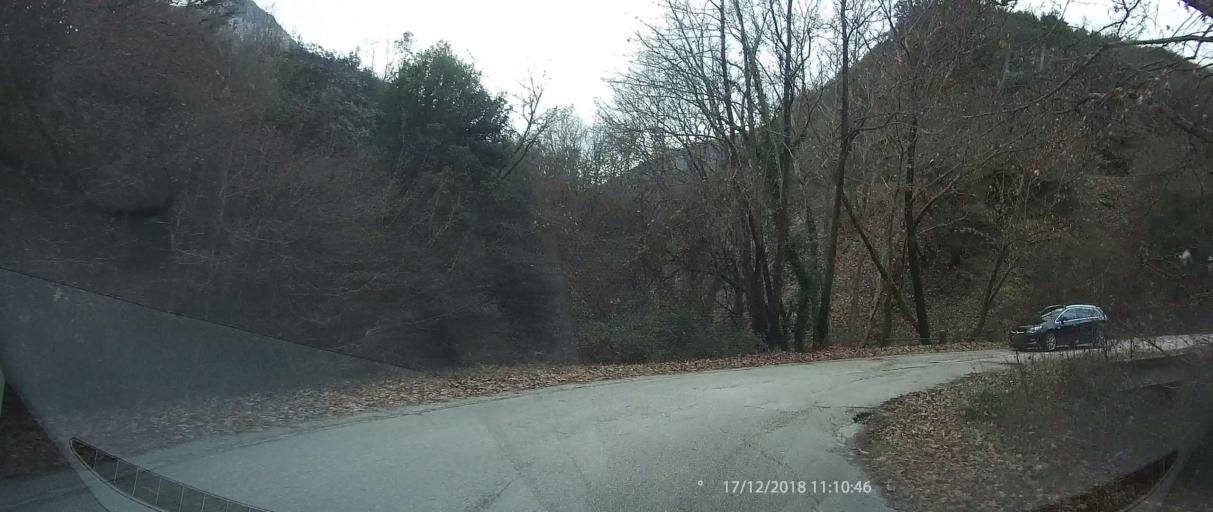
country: GR
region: Epirus
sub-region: Nomos Ioanninon
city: Kalpaki
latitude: 39.9429
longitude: 20.6814
